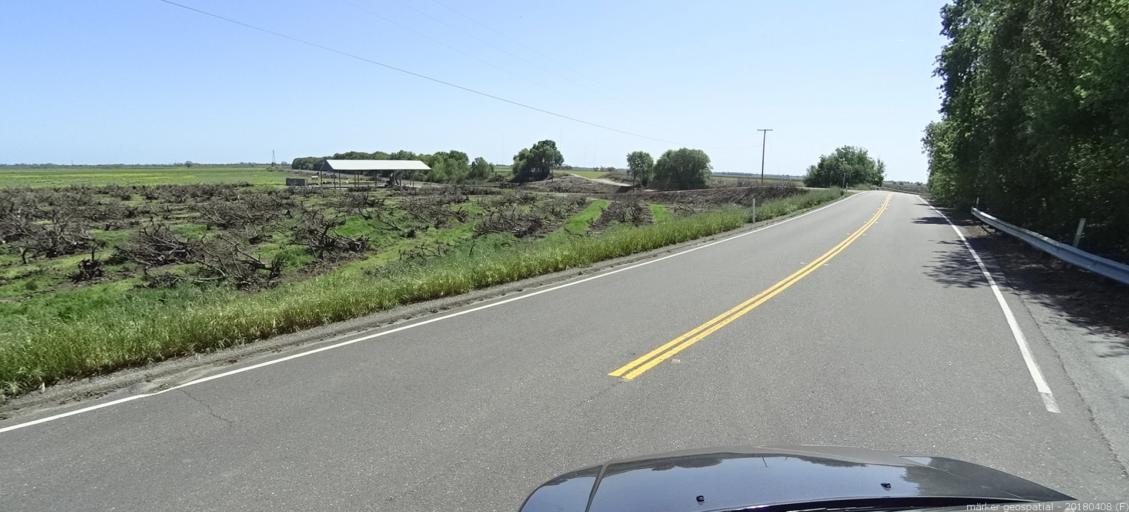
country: US
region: California
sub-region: Sacramento County
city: Walnut Grove
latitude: 38.3466
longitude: -121.5364
